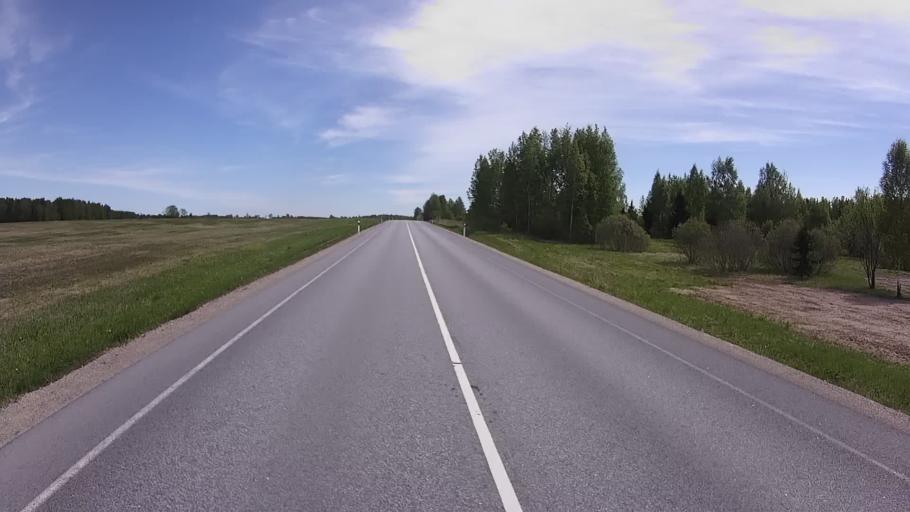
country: EE
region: Valgamaa
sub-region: Valga linn
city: Valga
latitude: 57.7240
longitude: 26.1878
